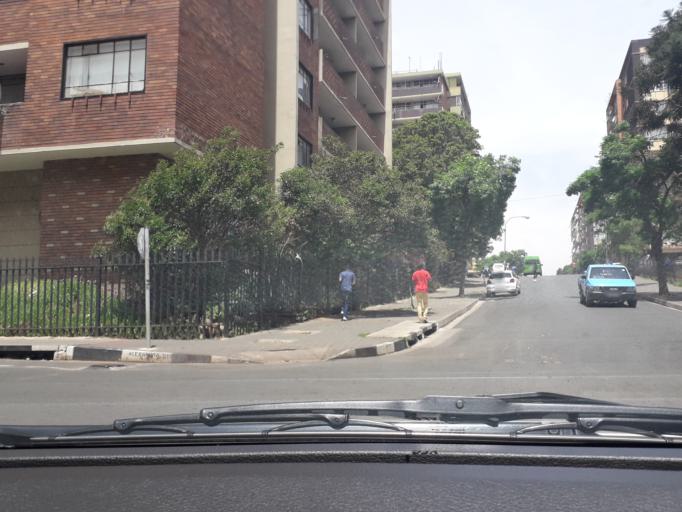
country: ZA
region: Gauteng
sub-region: City of Johannesburg Metropolitan Municipality
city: Johannesburg
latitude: -26.1865
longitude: 28.0522
